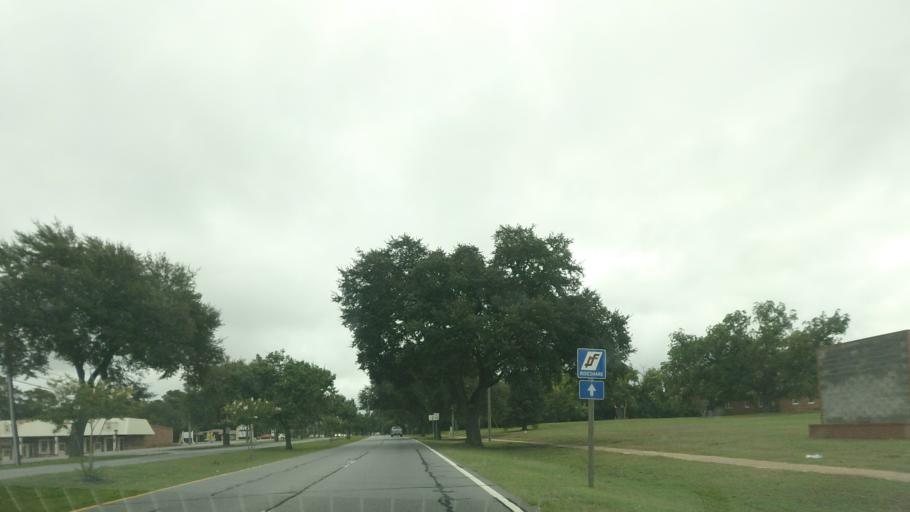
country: US
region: Georgia
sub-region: Laurens County
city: Dublin
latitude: 32.5378
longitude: -82.9388
